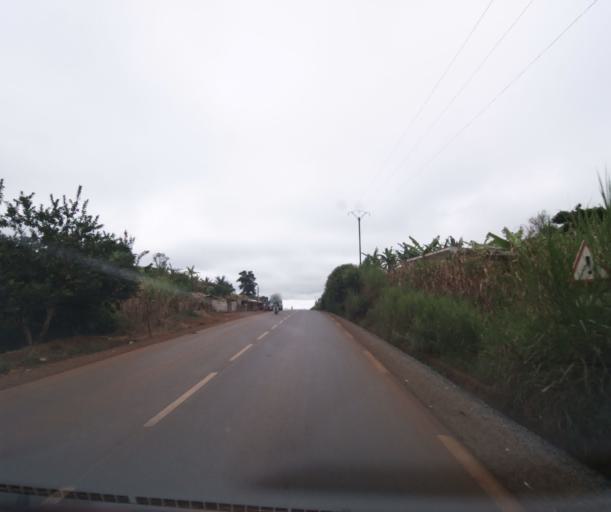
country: CM
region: West
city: Mbouda
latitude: 5.5583
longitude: 10.3159
